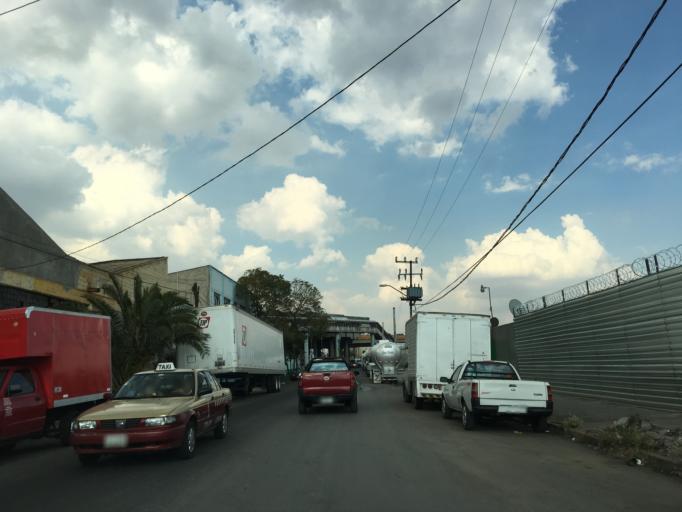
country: MX
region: Mexico City
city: Venustiano Carranza
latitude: 19.4395
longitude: -99.0946
